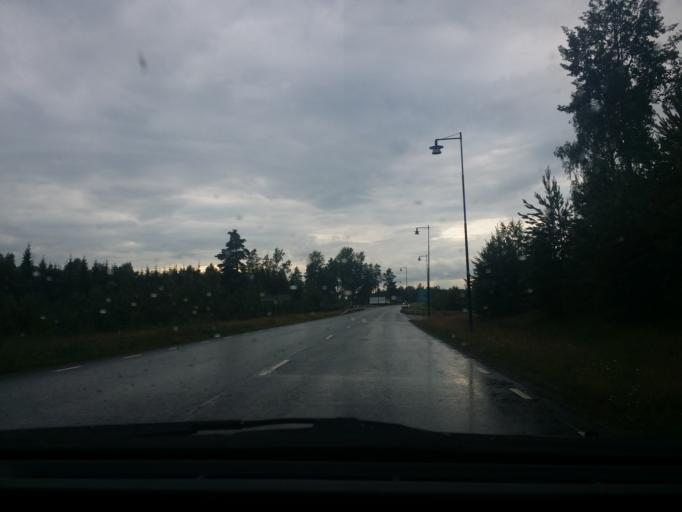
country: SE
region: Vaestmanland
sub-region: Arboga Kommun
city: Arboga
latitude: 59.4217
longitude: 15.8275
